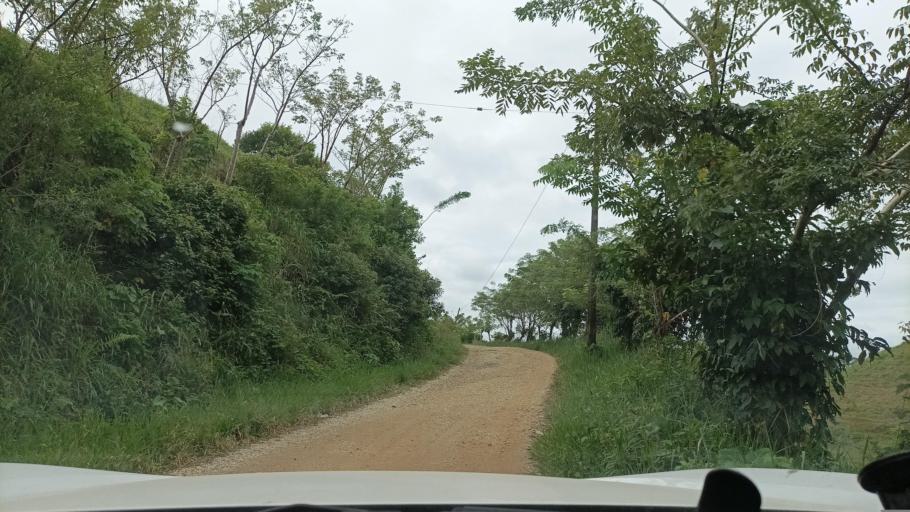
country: MX
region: Veracruz
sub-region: Uxpanapa
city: Poblado 10
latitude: 17.5629
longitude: -94.4243
